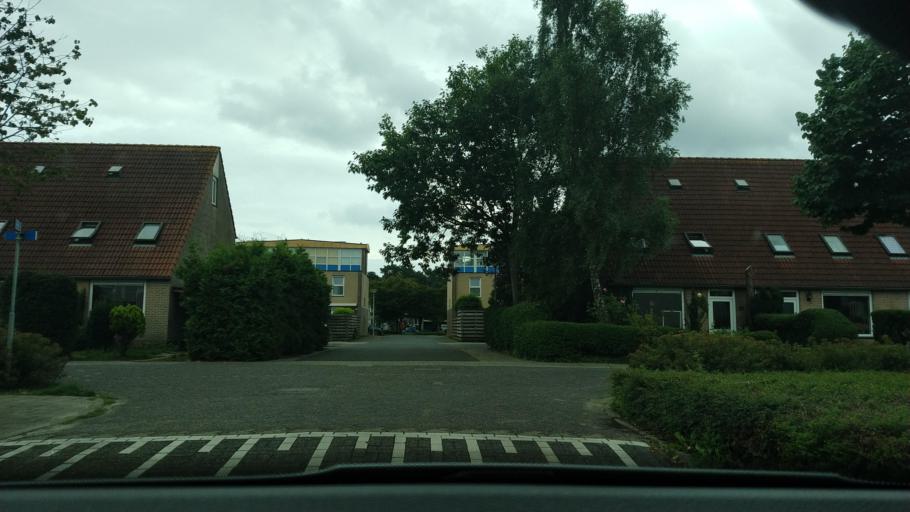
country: NL
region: Gelderland
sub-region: Gemeente Ermelo
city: Horst
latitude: 52.2911
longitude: 5.5988
